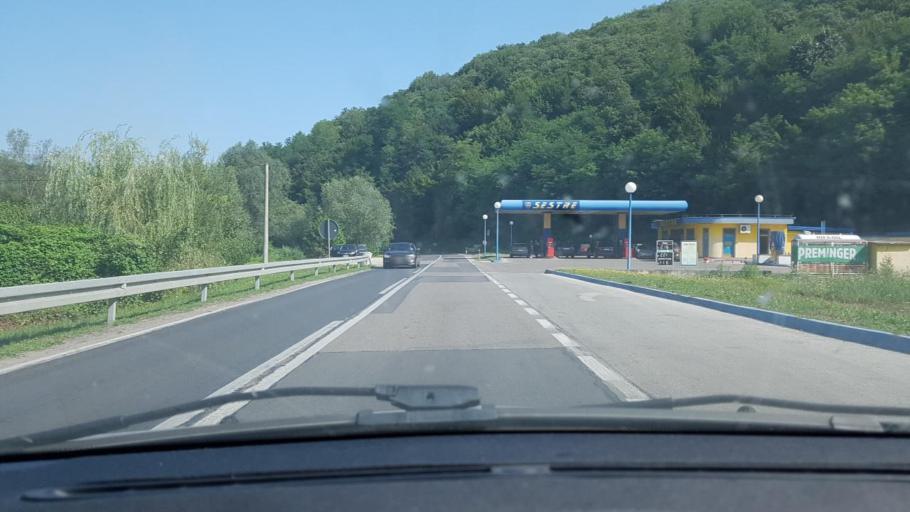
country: BA
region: Federation of Bosnia and Herzegovina
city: Sumatac
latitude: 45.1153
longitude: 15.8662
